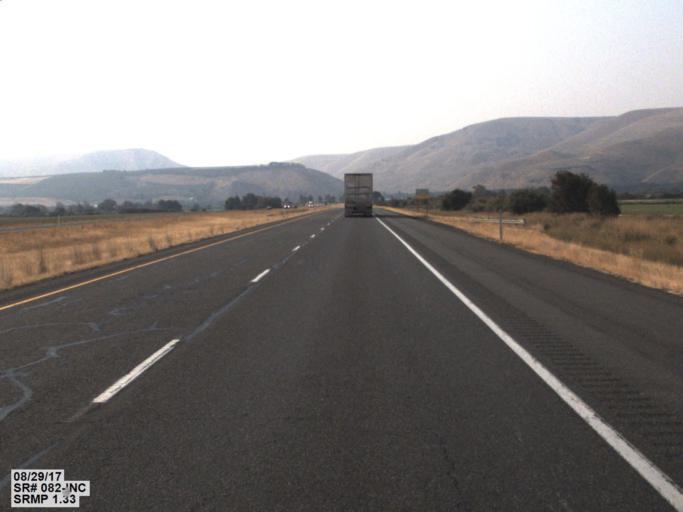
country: US
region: Washington
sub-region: Kittitas County
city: Ellensburg
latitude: 46.9524
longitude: -120.5079
